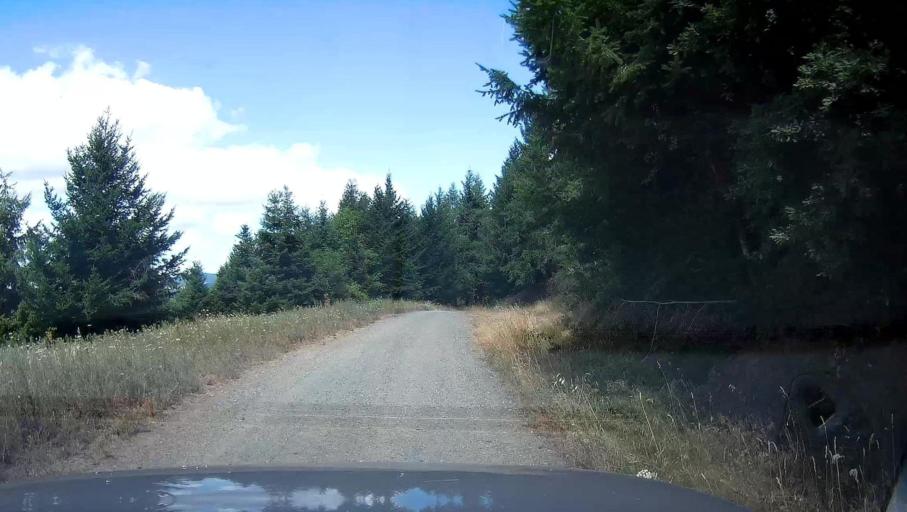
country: FR
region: Rhone-Alpes
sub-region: Departement du Rhone
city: Grandris
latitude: 46.0181
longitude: 4.5393
